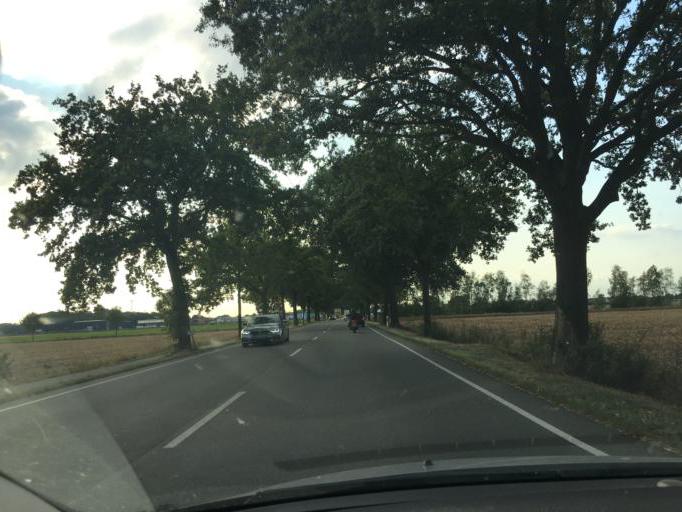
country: DE
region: Lower Saxony
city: Eicklingen
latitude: 52.5411
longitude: 10.2028
